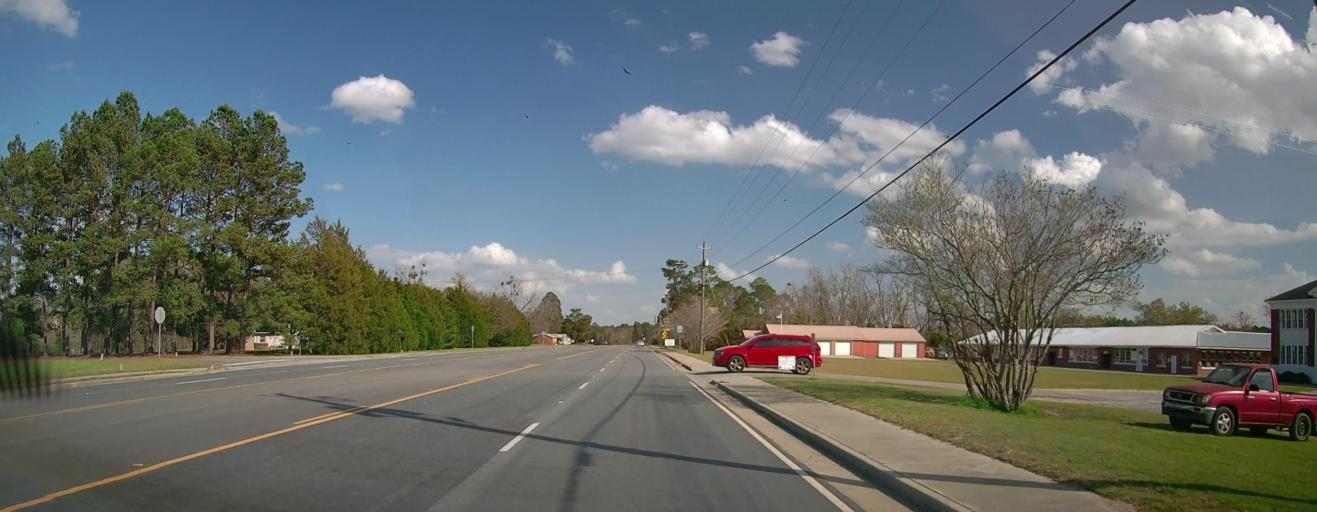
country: US
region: Georgia
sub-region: Telfair County
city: Helena
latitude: 32.1036
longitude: -83.0607
